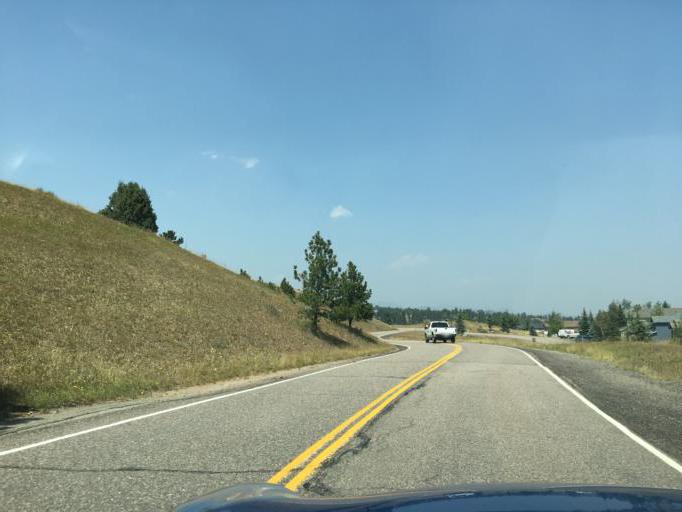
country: US
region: Colorado
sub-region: Jefferson County
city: Genesee
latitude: 39.7004
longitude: -105.2729
